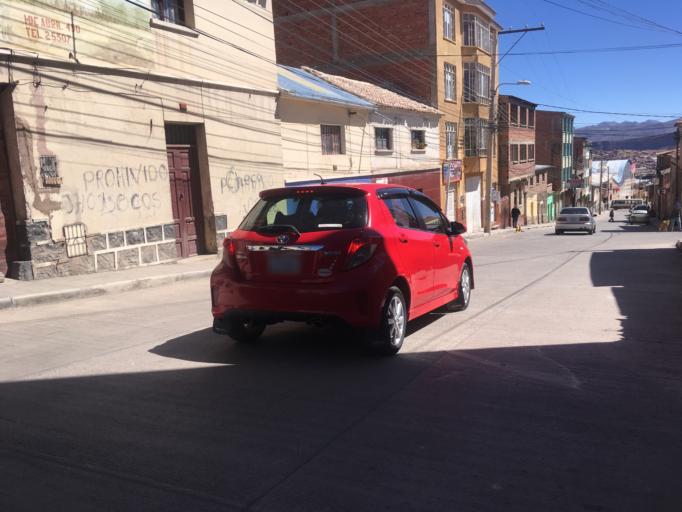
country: BO
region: Potosi
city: Potosi
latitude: -19.5818
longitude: -65.7549
